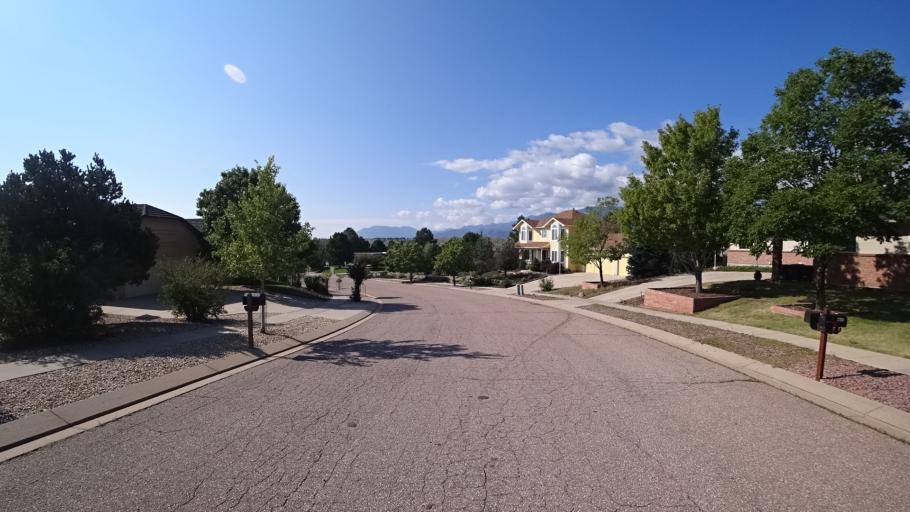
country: US
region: Colorado
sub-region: El Paso County
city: Manitou Springs
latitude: 38.9043
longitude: -104.8669
